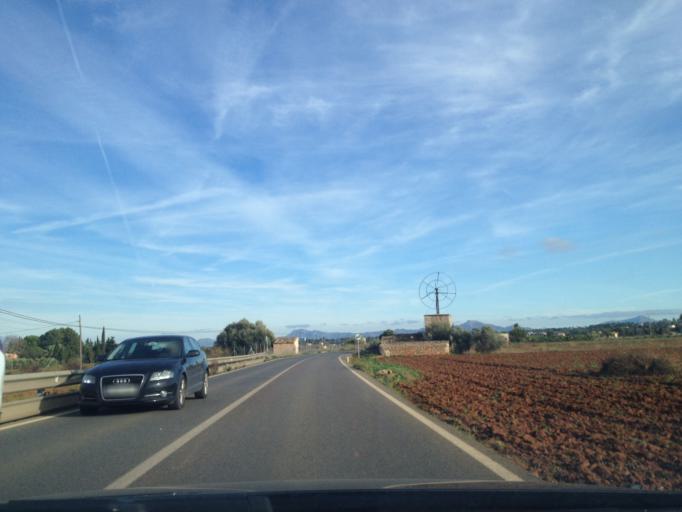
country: ES
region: Balearic Islands
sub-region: Illes Balears
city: Muro
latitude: 39.7656
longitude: 3.0985
